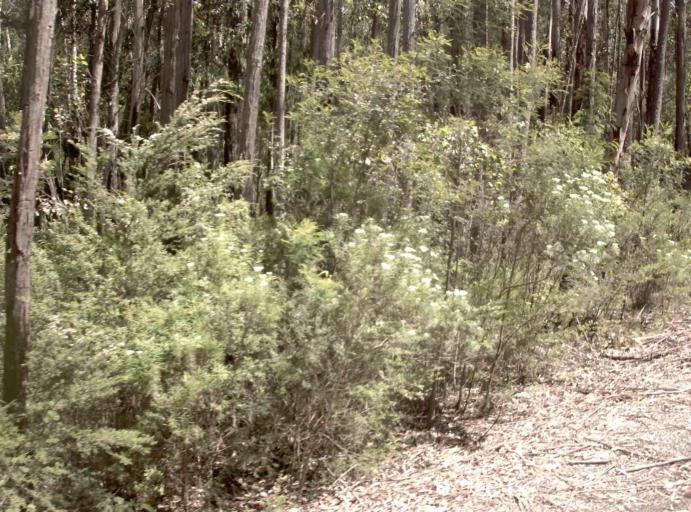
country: AU
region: Victoria
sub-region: East Gippsland
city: Lakes Entrance
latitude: -37.3624
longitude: 148.2208
